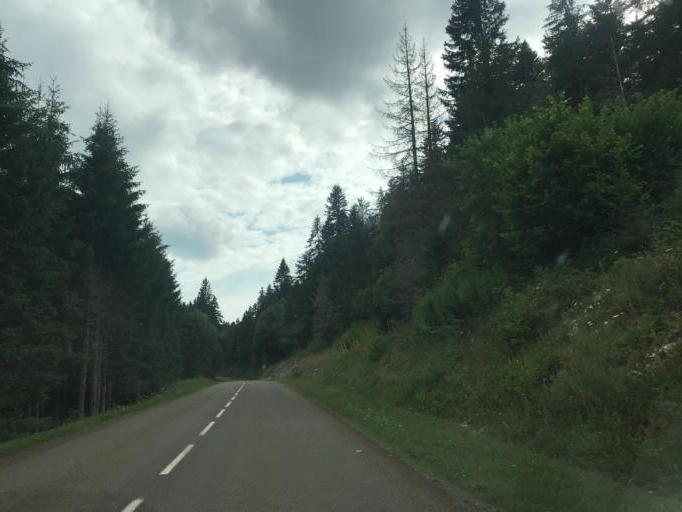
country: FR
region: Franche-Comte
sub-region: Departement du Jura
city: Valfin-les-Saint-Claude
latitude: 46.4950
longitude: 5.8507
